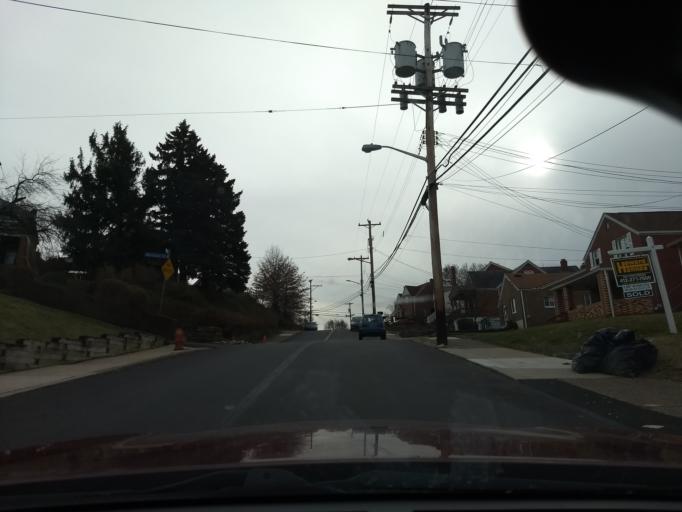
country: US
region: Pennsylvania
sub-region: Allegheny County
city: Homestead
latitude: 40.4201
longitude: -79.9376
